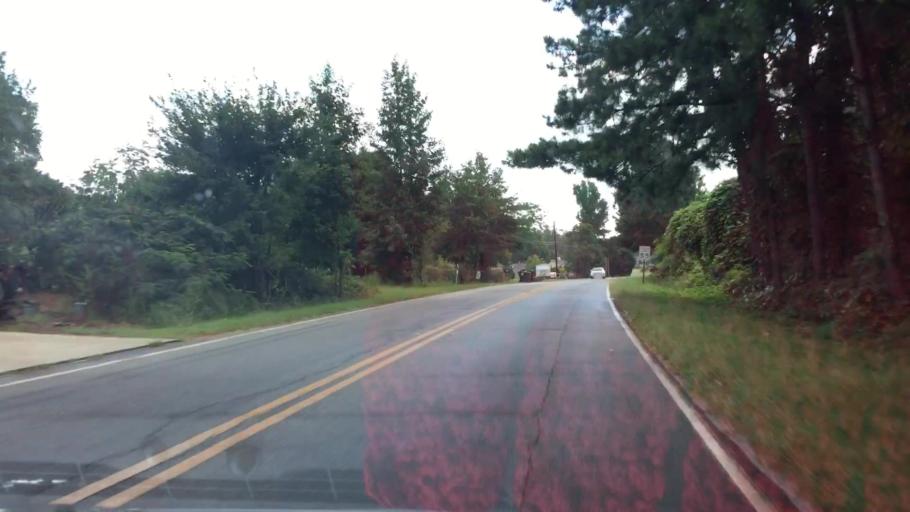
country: US
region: Georgia
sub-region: Clayton County
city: Lovejoy
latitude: 33.4235
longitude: -84.2847
